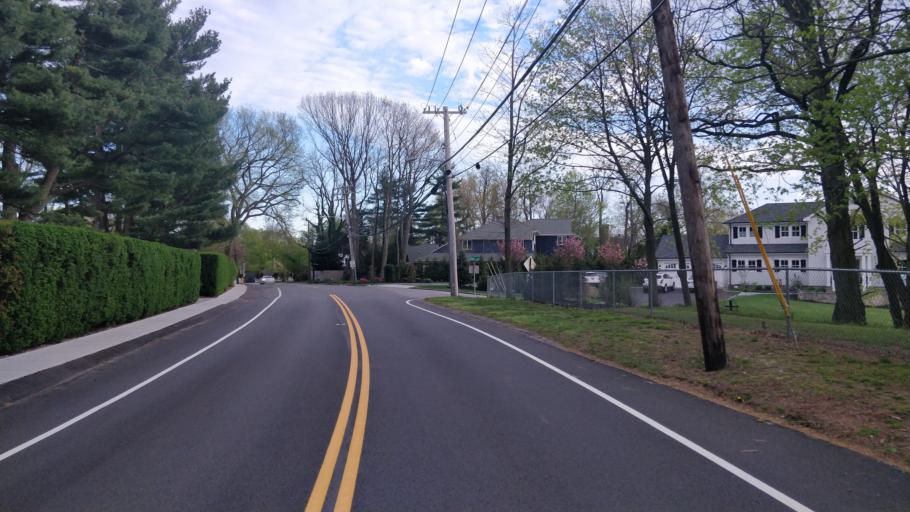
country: US
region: New York
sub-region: Suffolk County
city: Northport
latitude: 40.9099
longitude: -73.3449
